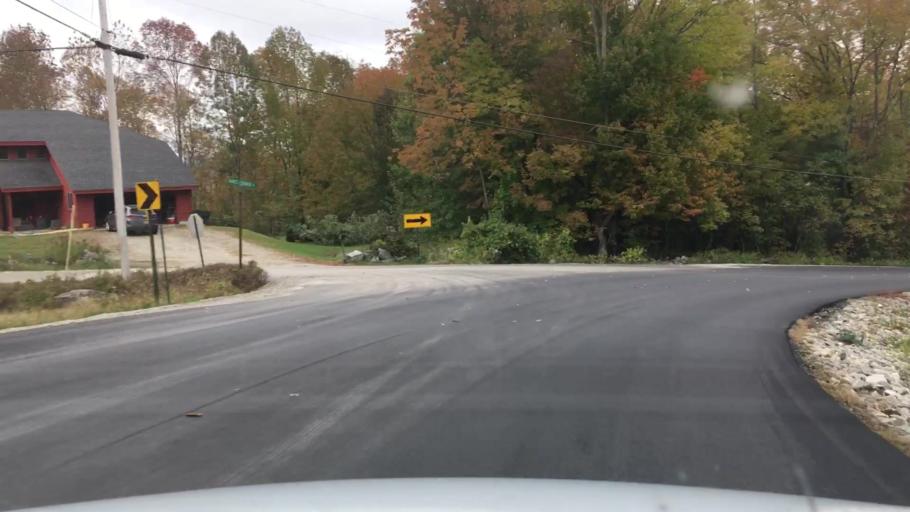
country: US
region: Maine
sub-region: Oxford County
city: Bethel
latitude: 44.3018
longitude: -70.7493
